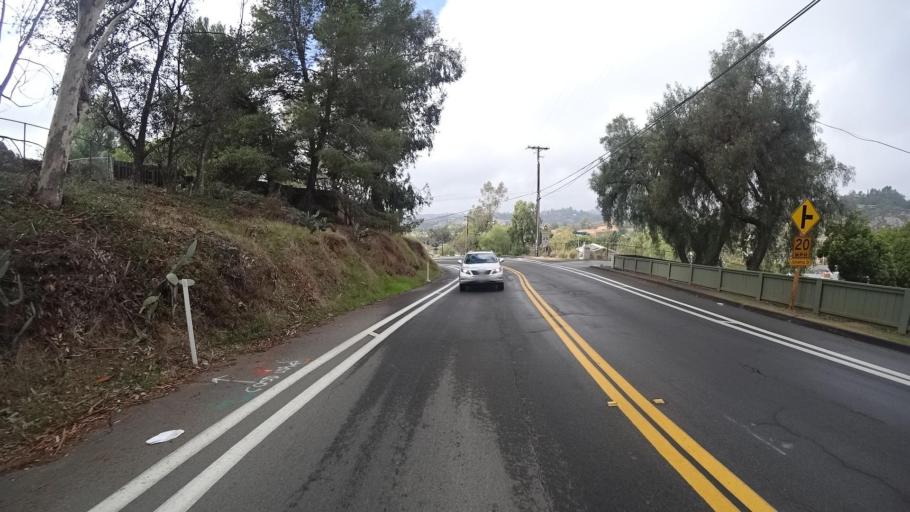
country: US
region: California
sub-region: San Diego County
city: Rancho San Diego
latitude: 32.7667
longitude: -116.9140
